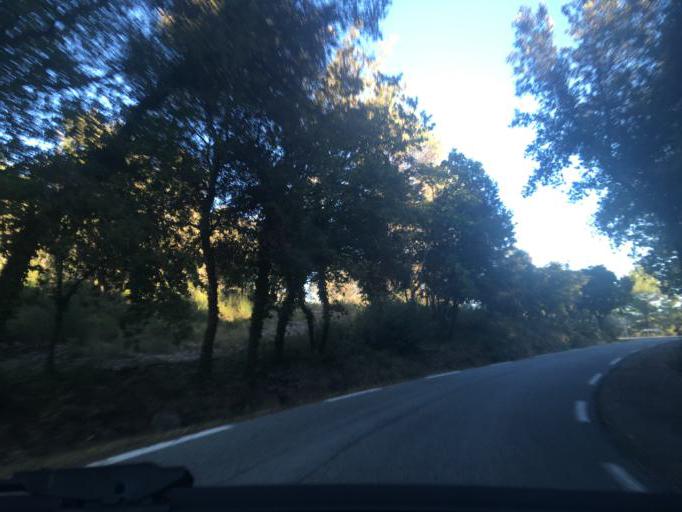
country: FR
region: Provence-Alpes-Cote d'Azur
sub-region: Departement du Var
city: Flayosc
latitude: 43.5626
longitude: 6.4079
